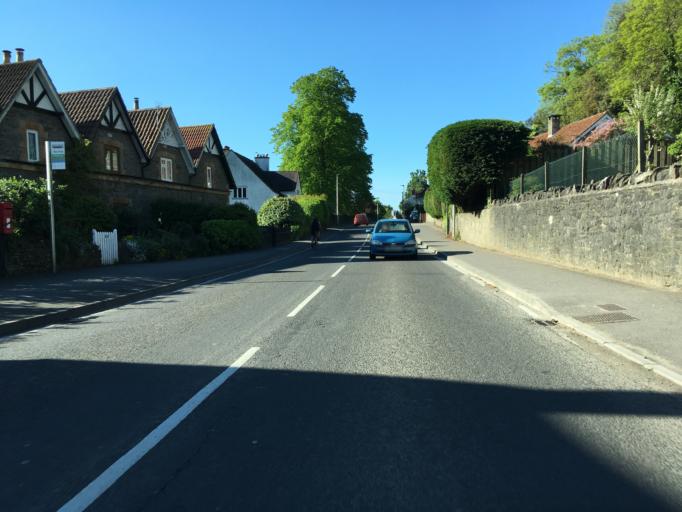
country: GB
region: England
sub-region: North Somerset
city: Clevedon
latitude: 51.4421
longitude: -2.8416
